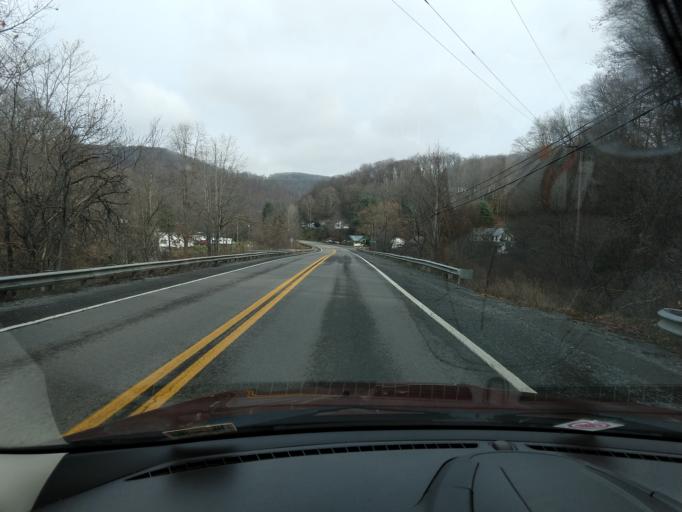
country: US
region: West Virginia
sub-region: Greenbrier County
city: Rainelle
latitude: 38.0467
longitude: -80.7223
